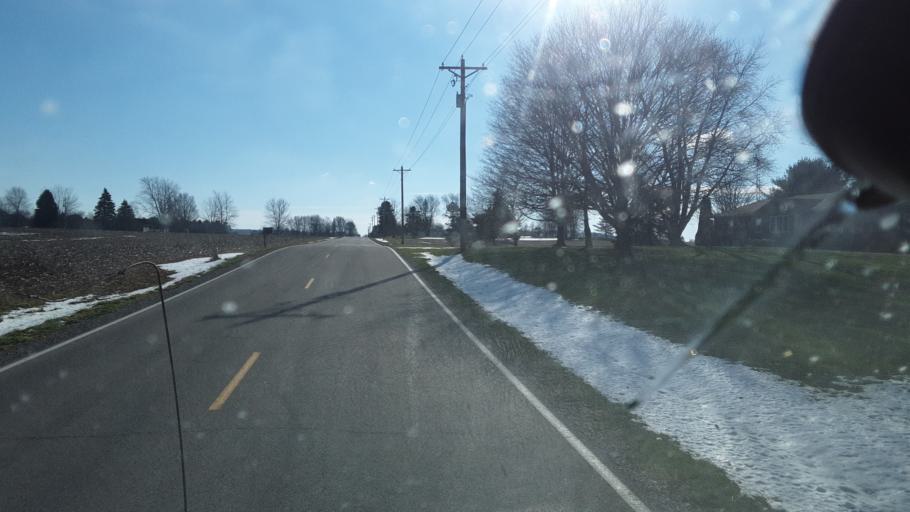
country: US
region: Ohio
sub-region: Huron County
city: Plymouth
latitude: 40.9549
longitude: -82.7433
